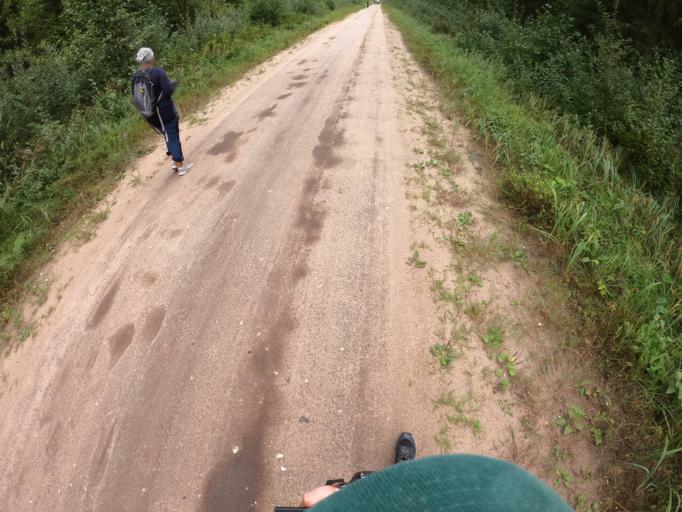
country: LV
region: Engure
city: Smarde
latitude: 56.9964
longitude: 23.3849
